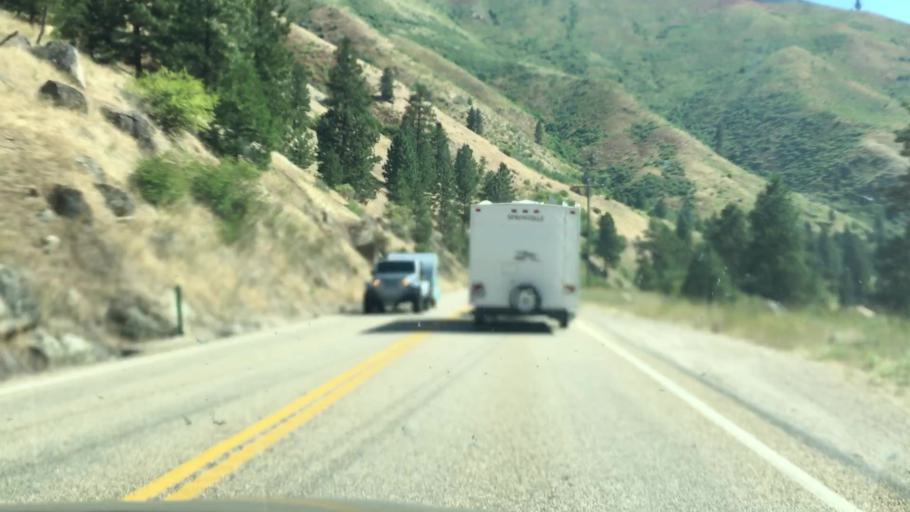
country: US
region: Idaho
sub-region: Boise County
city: Idaho City
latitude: 44.0330
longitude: -116.1342
